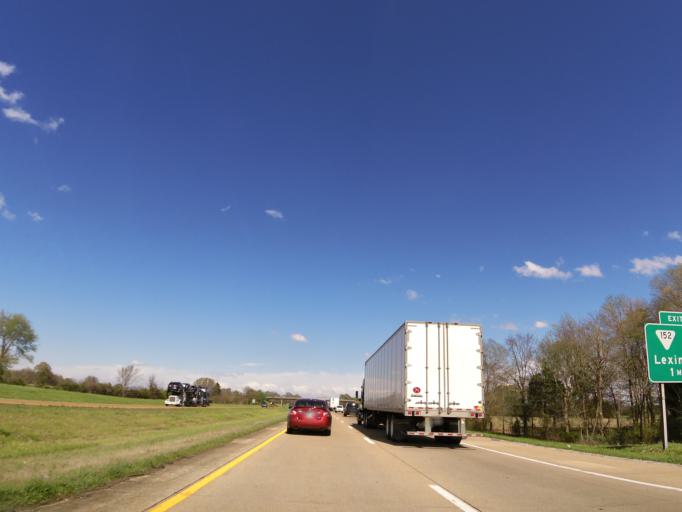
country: US
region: Tennessee
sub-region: Gibson County
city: Medina
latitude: 35.7119
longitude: -88.6540
